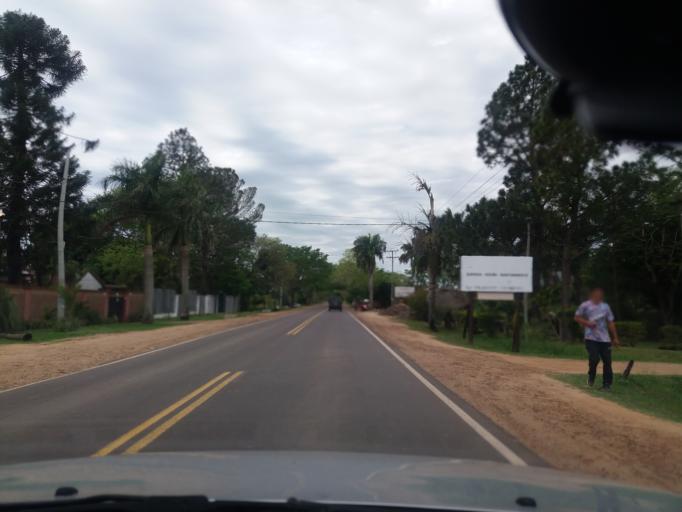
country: AR
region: Corrientes
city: Corrientes
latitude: -27.4488
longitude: -58.7492
